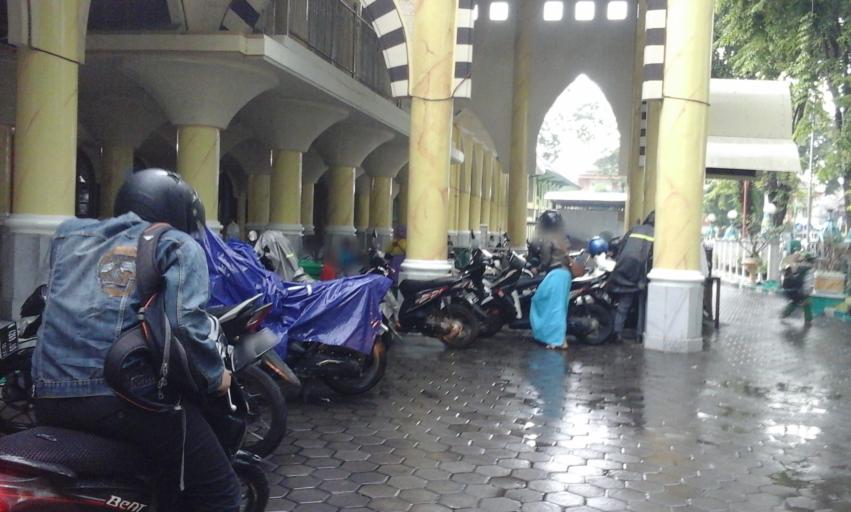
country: ID
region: East Java
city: Lumajang
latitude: -8.1349
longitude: 113.2233
